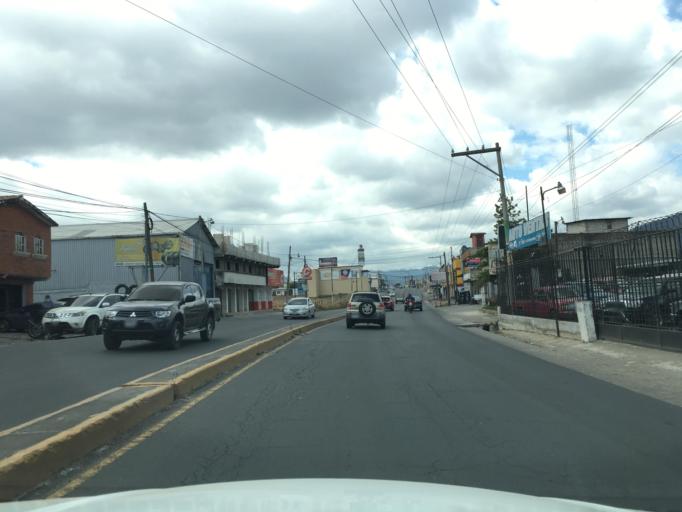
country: GT
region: Quetzaltenango
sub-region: Municipio de La Esperanza
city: La Esperanza
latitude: 14.8670
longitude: -91.5701
